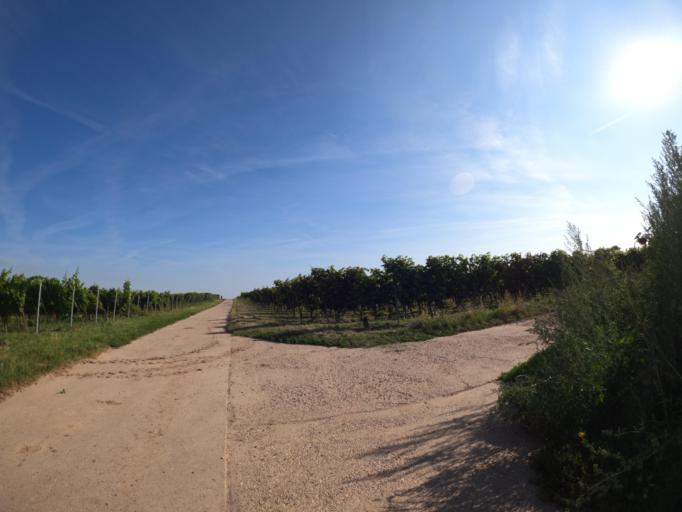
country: DE
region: Rheinland-Pfalz
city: Bissersheim
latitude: 49.5326
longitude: 8.2026
